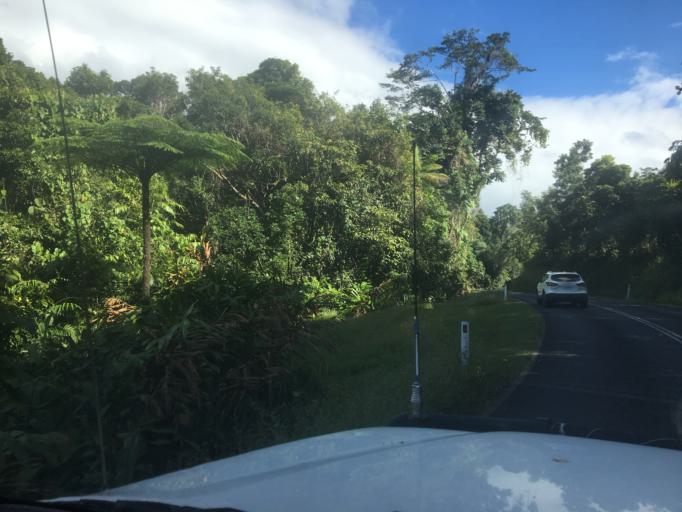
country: AU
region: Queensland
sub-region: Cassowary Coast
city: Innisfail
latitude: -17.3435
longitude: 145.8737
